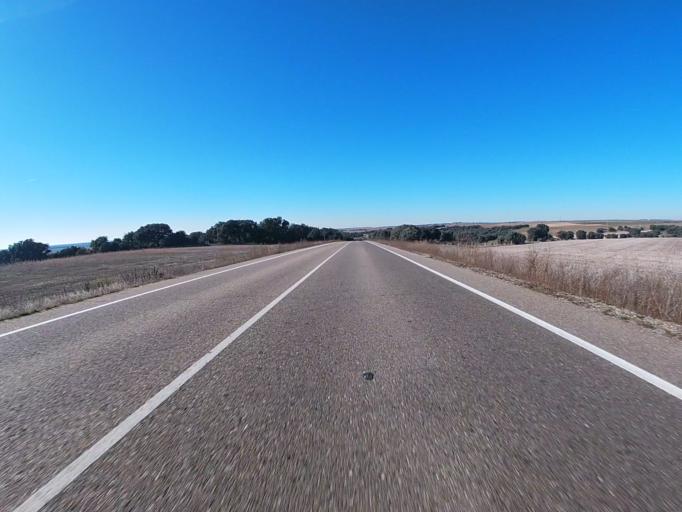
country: ES
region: Castille and Leon
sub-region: Provincia de Salamanca
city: Almenara de Tormes
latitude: 41.0762
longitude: -5.8384
